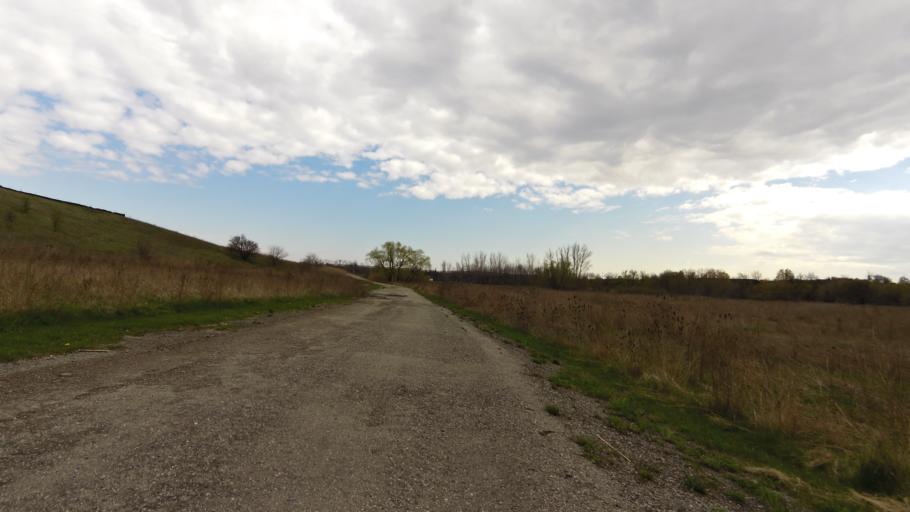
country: CA
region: Ontario
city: Etobicoke
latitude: 43.6689
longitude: -79.6379
